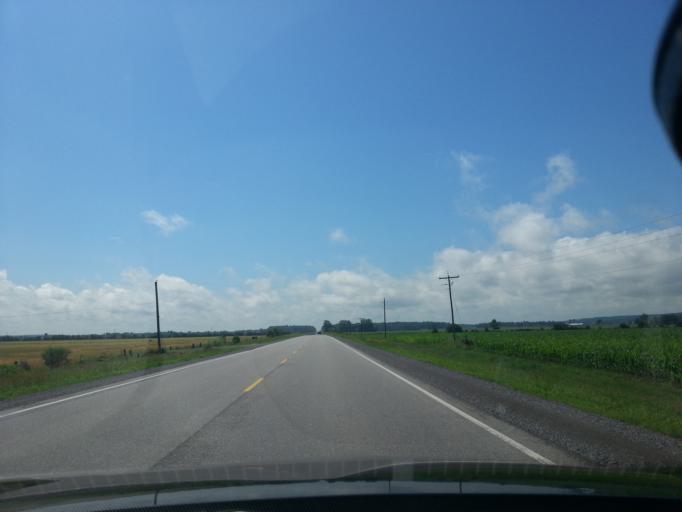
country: CA
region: Ontario
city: Renfrew
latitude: 45.5152
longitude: -76.8004
